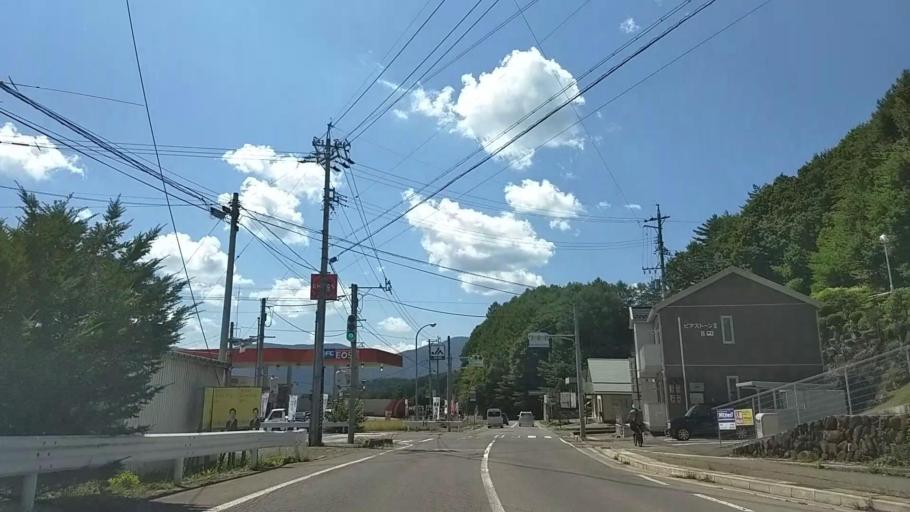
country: JP
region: Nagano
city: Chino
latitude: 36.0152
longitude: 138.1883
